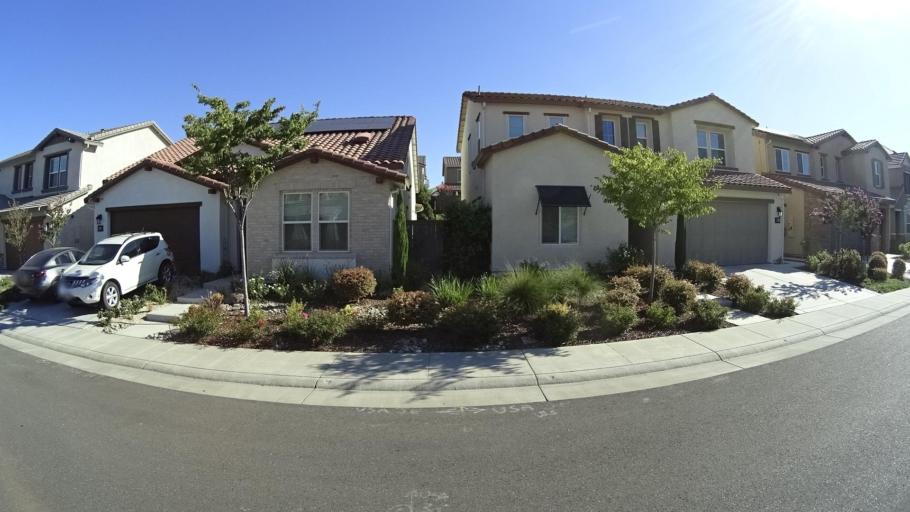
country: US
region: California
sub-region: Placer County
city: Rocklin
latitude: 38.8282
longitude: -121.2697
